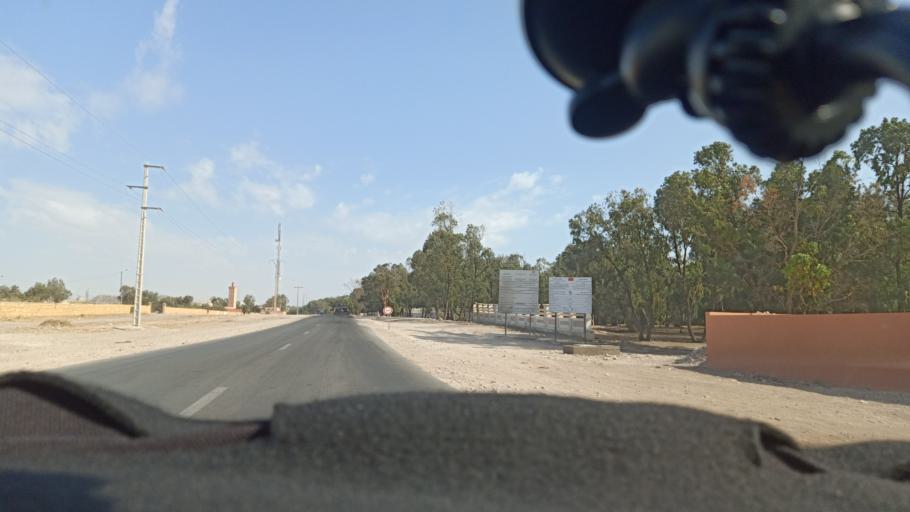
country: MA
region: Doukkala-Abda
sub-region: Safi
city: Youssoufia
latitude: 32.2727
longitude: -8.5372
